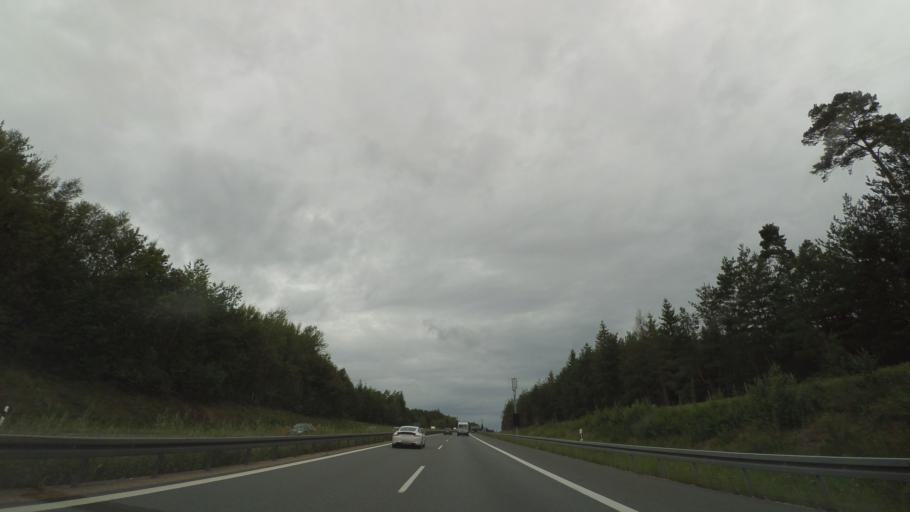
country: DE
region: Bavaria
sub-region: Upper Palatinate
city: Kummersbruck
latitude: 49.3933
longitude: 11.8764
